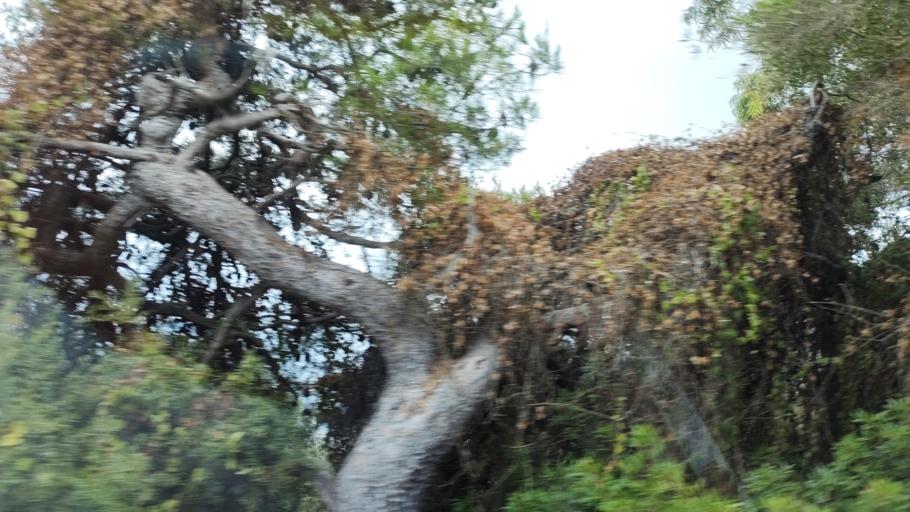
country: GI
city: Gibraltar
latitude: 36.1221
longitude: -5.3462
